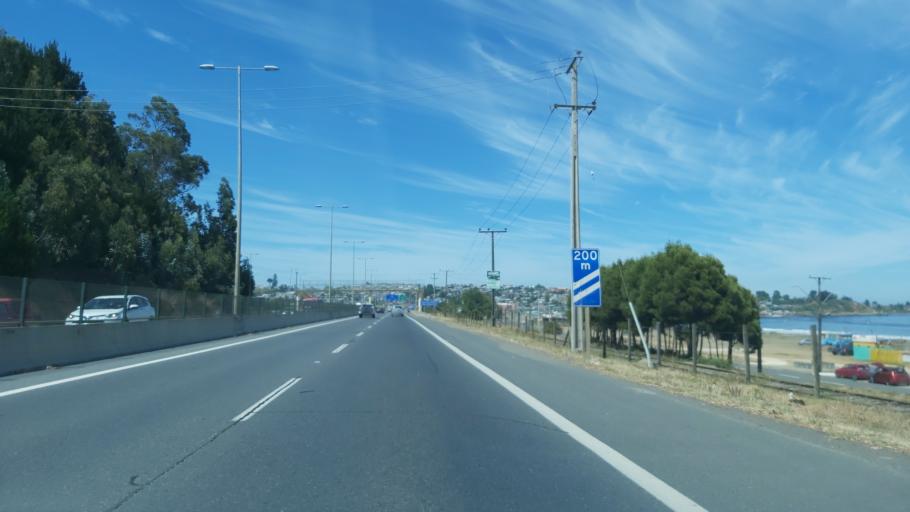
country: CL
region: Biobio
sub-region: Provincia de Concepcion
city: Lota
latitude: -37.0651
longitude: -73.1427
